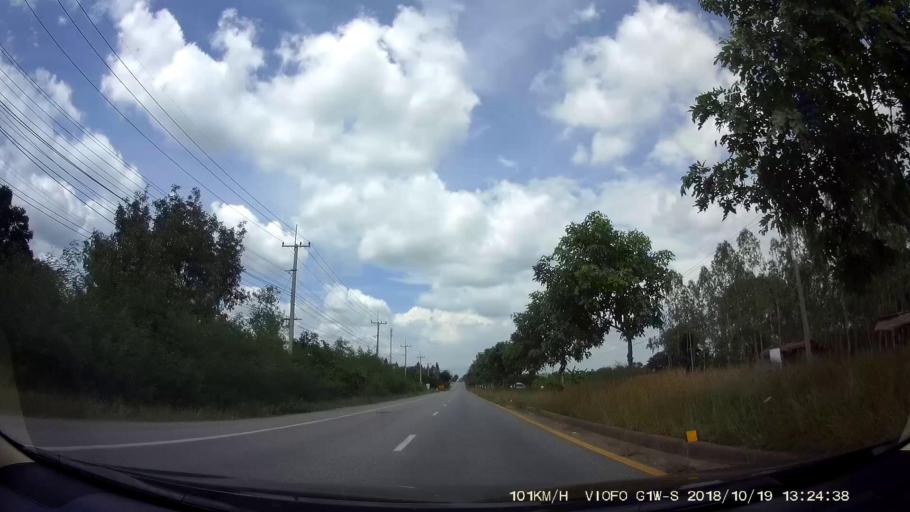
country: TH
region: Chaiyaphum
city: Chatturat
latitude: 15.5097
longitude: 101.8223
